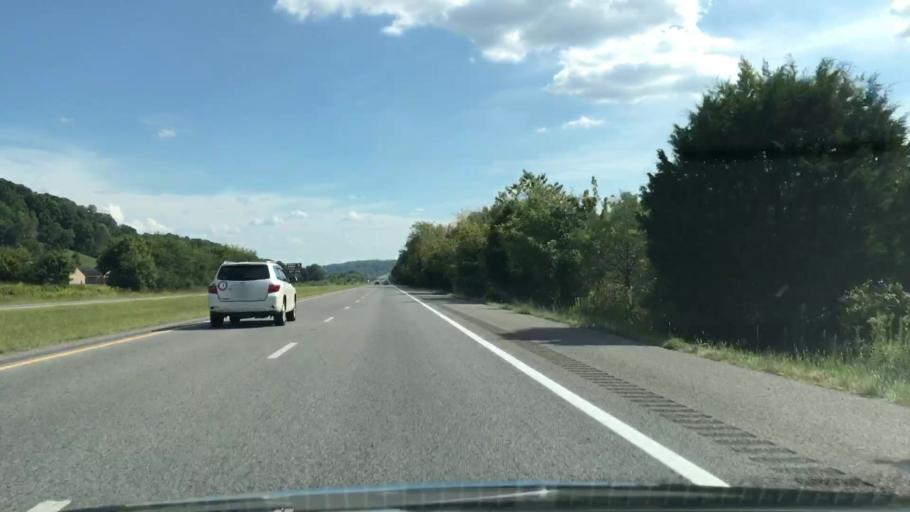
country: US
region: Tennessee
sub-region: Giles County
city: Pulaski
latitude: 35.1574
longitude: -86.8799
